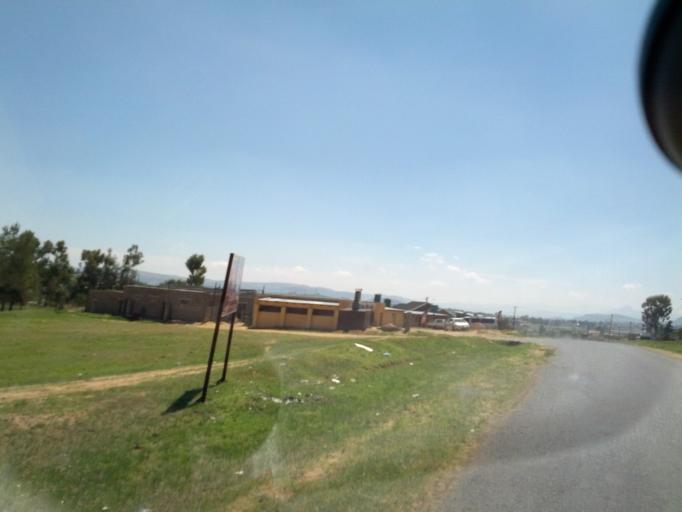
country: LS
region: Butha-Buthe
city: Butha-Buthe
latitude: -28.7787
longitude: 28.2303
